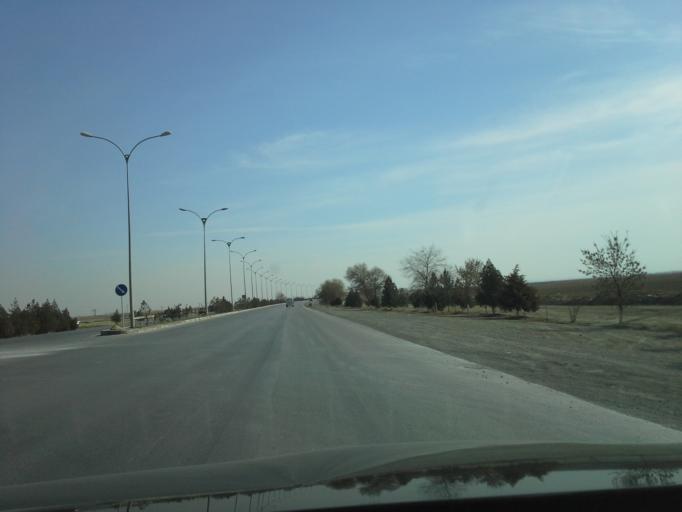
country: TM
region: Ahal
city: Abadan
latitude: 38.1354
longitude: 58.0109
